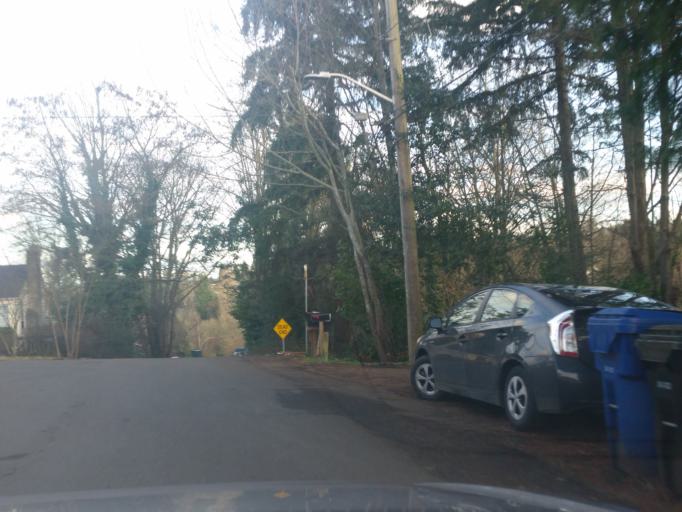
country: US
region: Washington
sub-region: King County
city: Lake Forest Park
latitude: 47.7021
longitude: -122.3047
